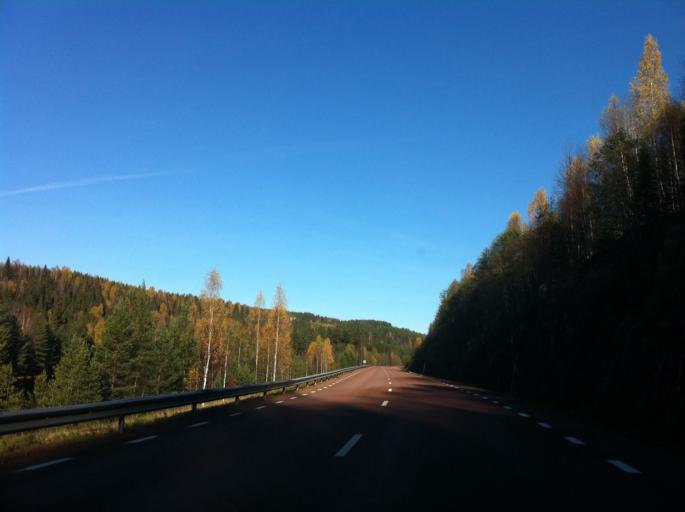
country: SE
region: Dalarna
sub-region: Alvdalens Kommun
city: AElvdalen
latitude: 61.2699
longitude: 13.8352
